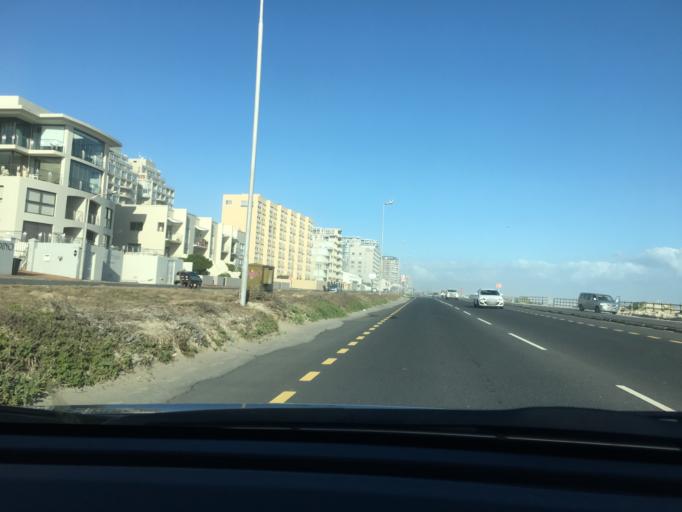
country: ZA
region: Western Cape
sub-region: City of Cape Town
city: Sunset Beach
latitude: -33.8171
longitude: 18.4736
